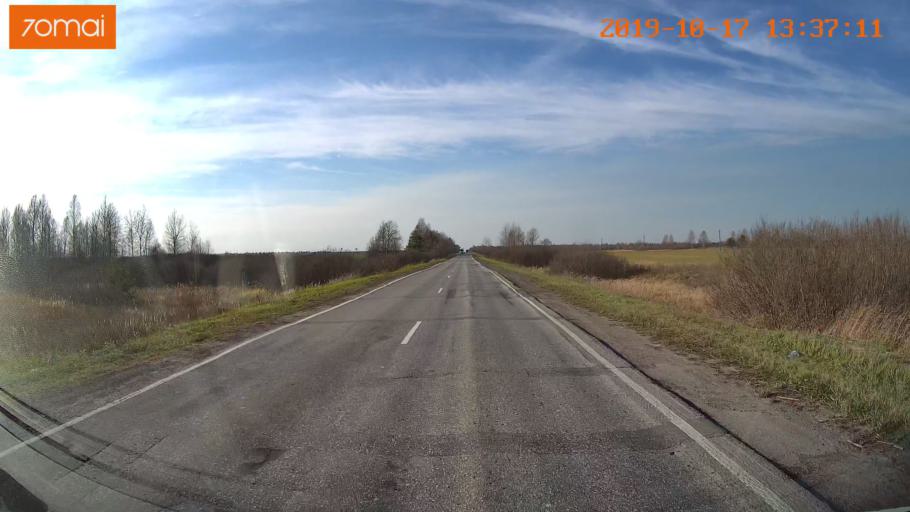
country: RU
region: Rjazan
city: Tuma
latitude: 55.1410
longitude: 40.6453
